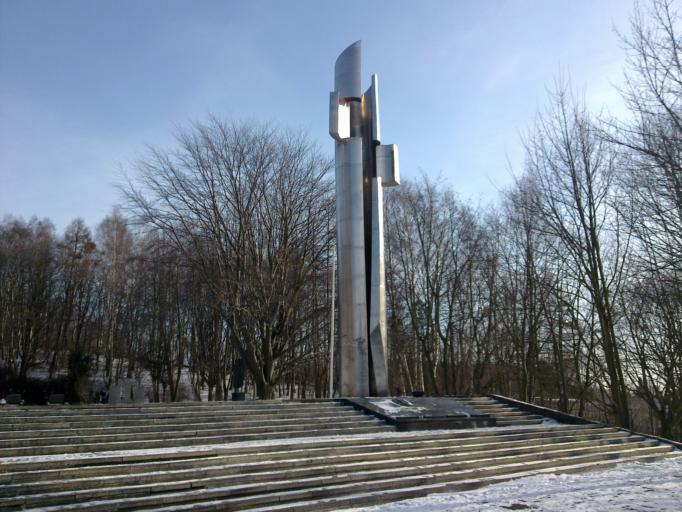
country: PL
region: Pomeranian Voivodeship
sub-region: Gdynia
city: Gdynia
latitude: 54.4906
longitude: 18.5450
